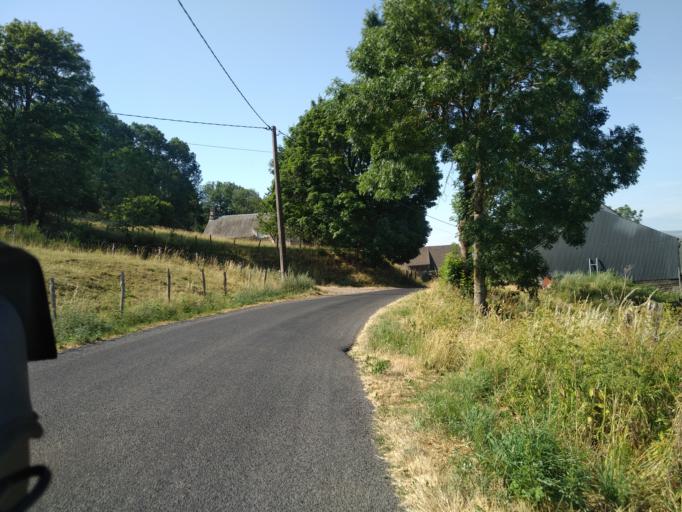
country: FR
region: Auvergne
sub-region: Departement du Cantal
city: Riom-es-Montagnes
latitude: 45.2462
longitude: 2.7427
